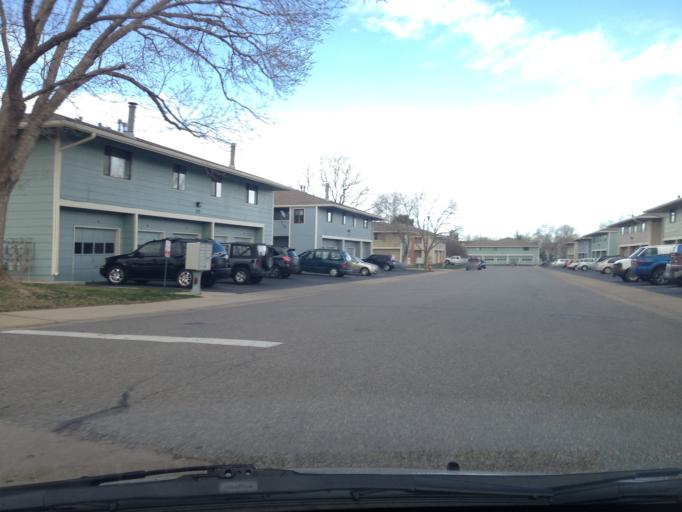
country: US
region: Colorado
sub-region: Boulder County
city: Lafayette
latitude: 39.9837
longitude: -105.1073
